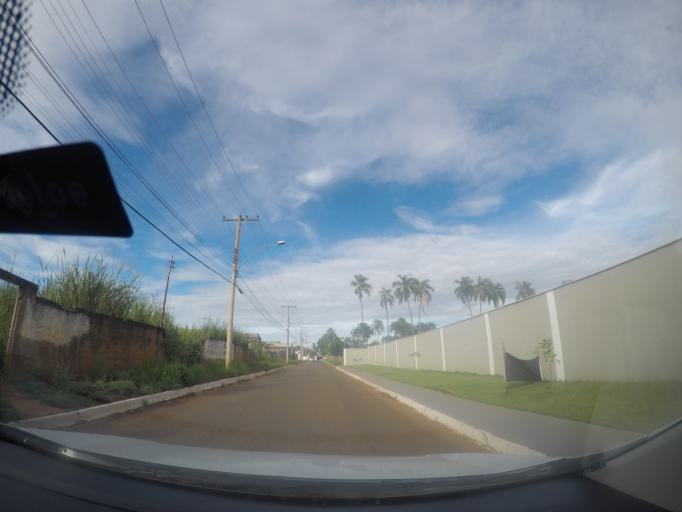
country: BR
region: Goias
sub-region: Goiania
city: Goiania
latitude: -16.6416
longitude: -49.3482
